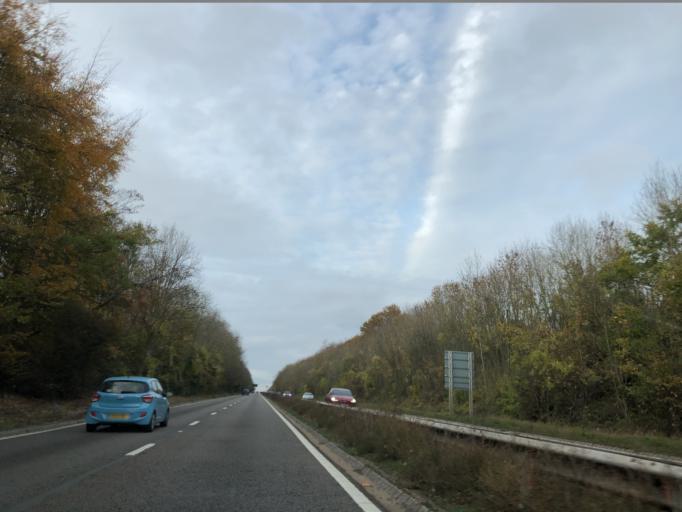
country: GB
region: England
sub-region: Buckinghamshire
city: Marlow
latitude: 51.5955
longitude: -0.7608
